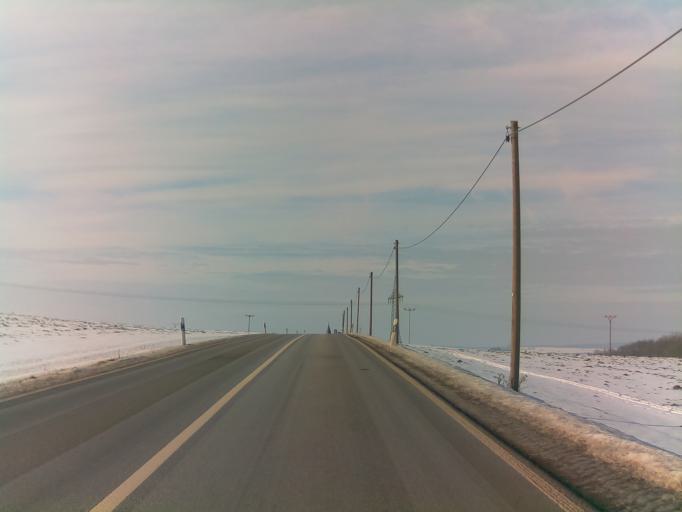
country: DE
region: Thuringia
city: Bucha
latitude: 50.8545
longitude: 11.5133
